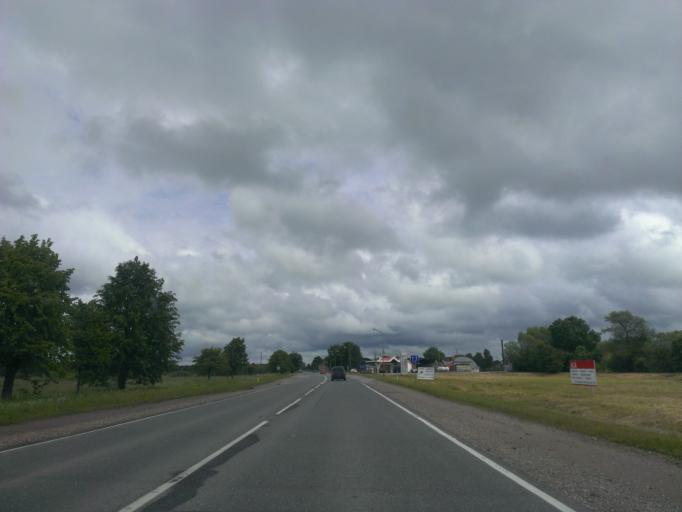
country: LV
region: Grobina
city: Grobina
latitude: 56.5359
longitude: 21.1397
